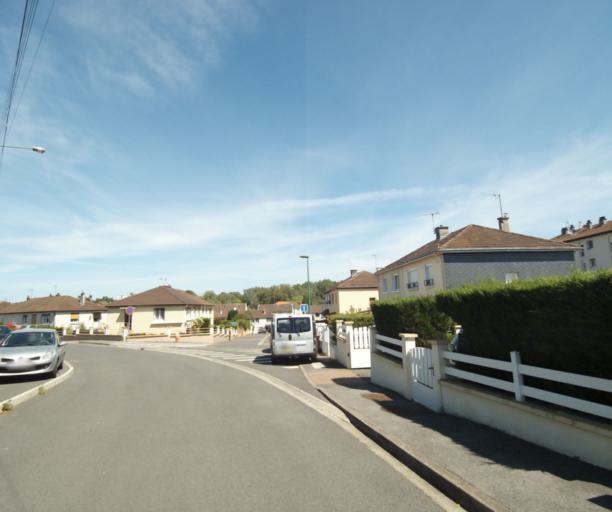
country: FR
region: Champagne-Ardenne
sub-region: Departement des Ardennes
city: La Francheville
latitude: 49.7473
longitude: 4.7168
